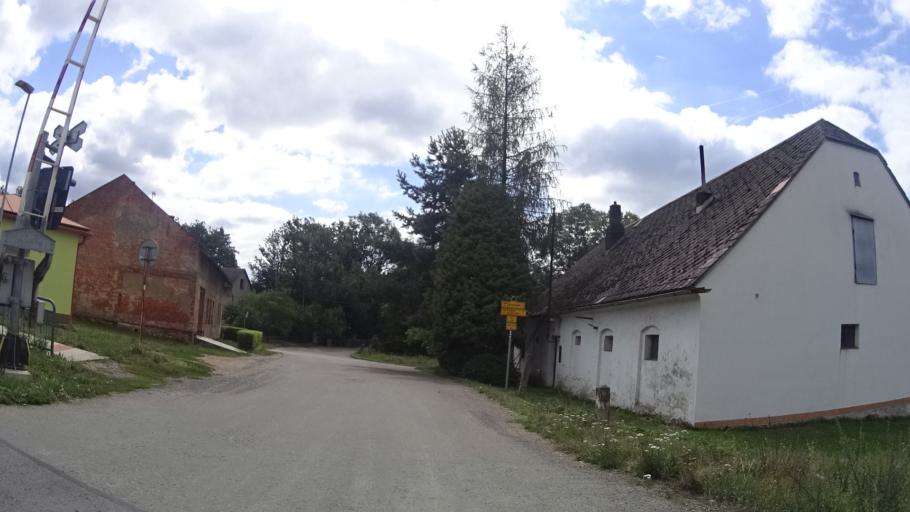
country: CZ
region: Pardubicky
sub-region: Okres Usti nad Orlici
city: Usti nad Orlici
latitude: 49.9894
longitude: 16.3968
